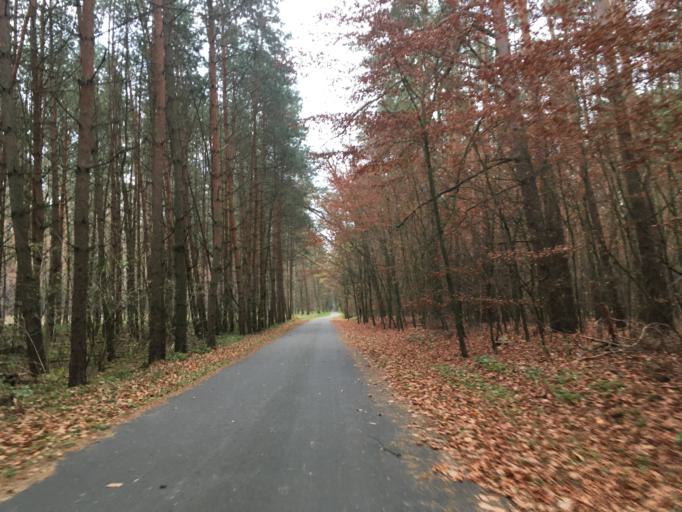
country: DE
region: Brandenburg
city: Neuhardenberg
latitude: 52.5812
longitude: 14.2468
